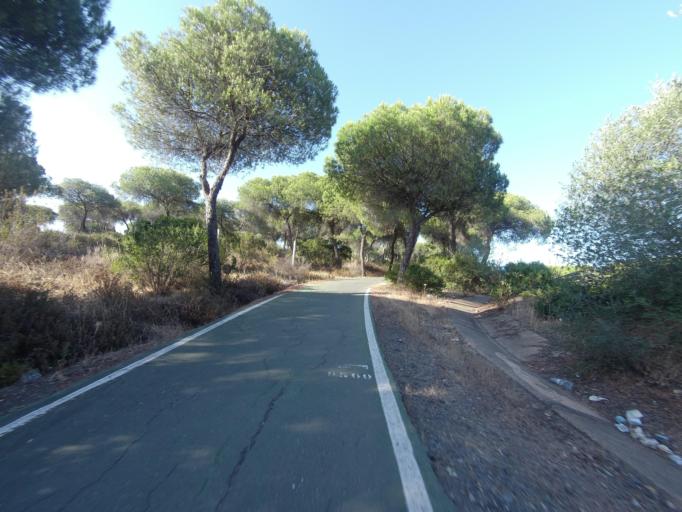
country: ES
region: Andalusia
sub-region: Provincia de Huelva
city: Aljaraque
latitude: 37.2313
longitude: -7.0191
